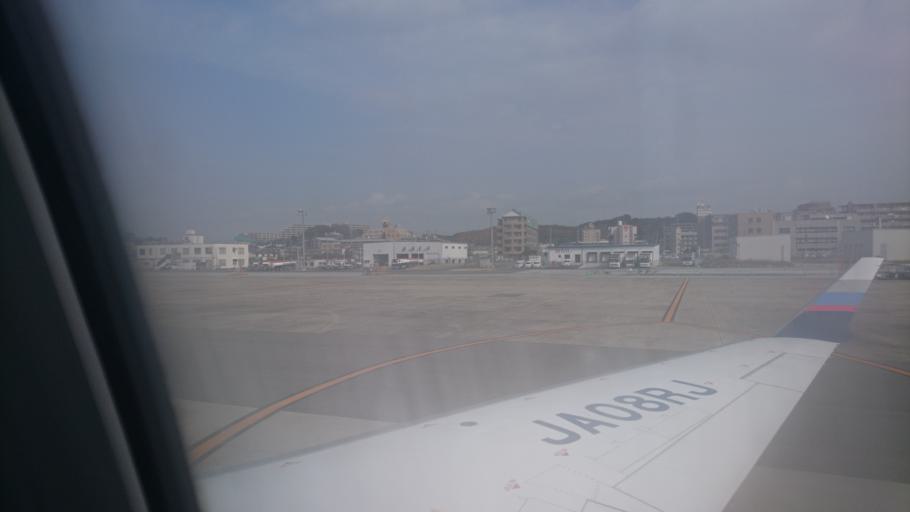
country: JP
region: Fukuoka
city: Fukuoka-shi
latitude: 33.5874
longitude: 130.4520
